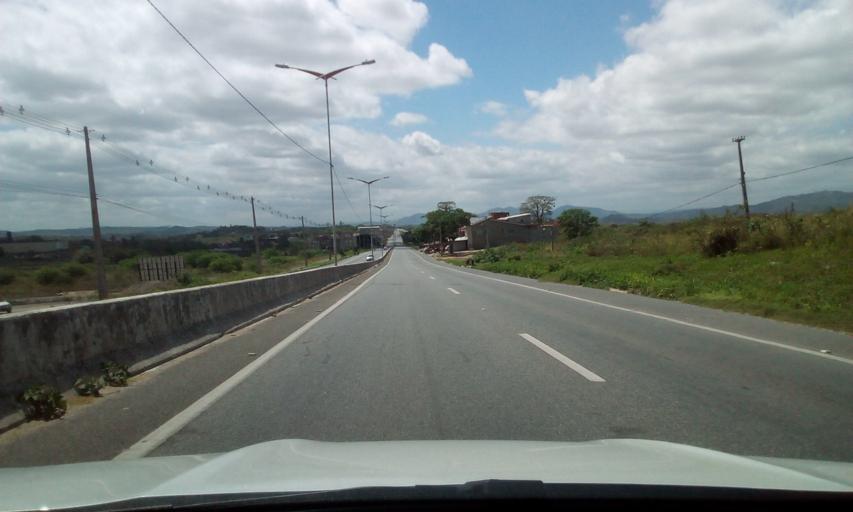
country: BR
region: Paraiba
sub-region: Campina Grande
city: Campina Grande
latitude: -7.2404
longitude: -35.8611
